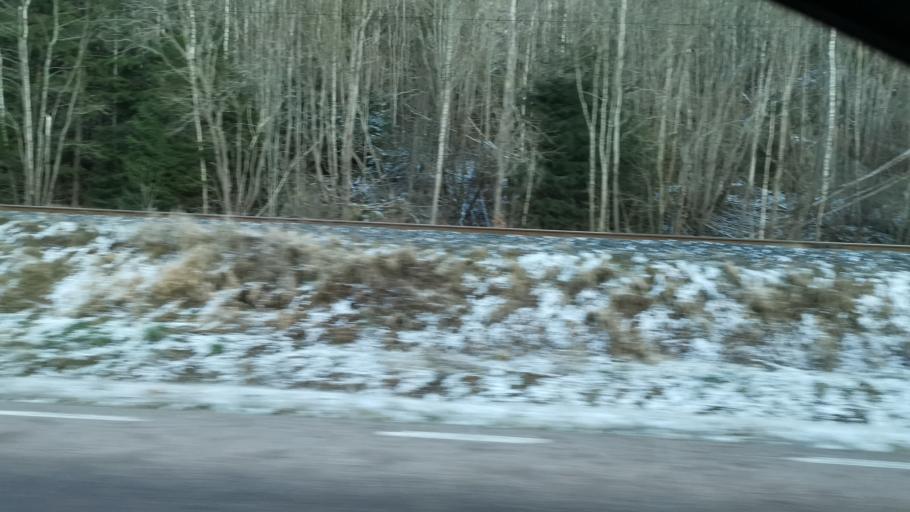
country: SE
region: Vaestra Goetaland
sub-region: Munkedals Kommun
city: Munkedal
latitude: 58.4163
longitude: 11.7323
